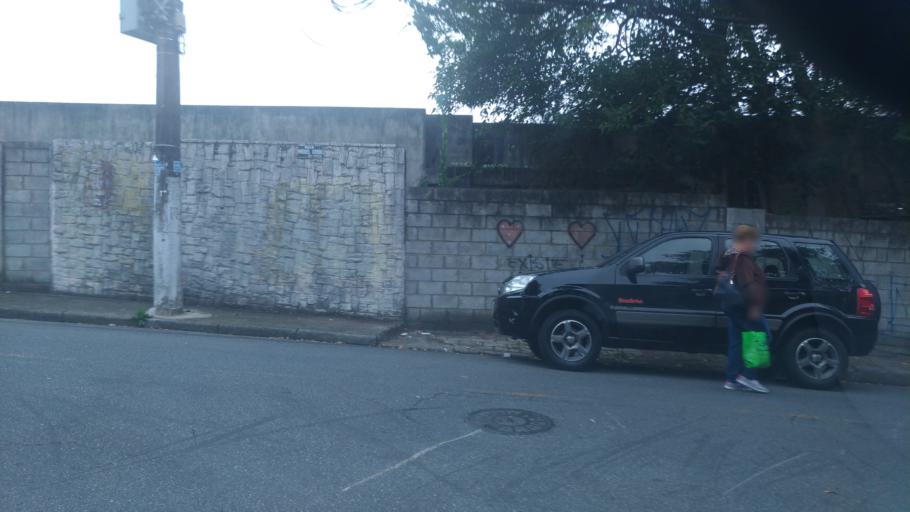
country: BR
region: Sao Paulo
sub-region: Sao Bernardo Do Campo
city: Sao Bernardo do Campo
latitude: -23.6988
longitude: -46.5589
